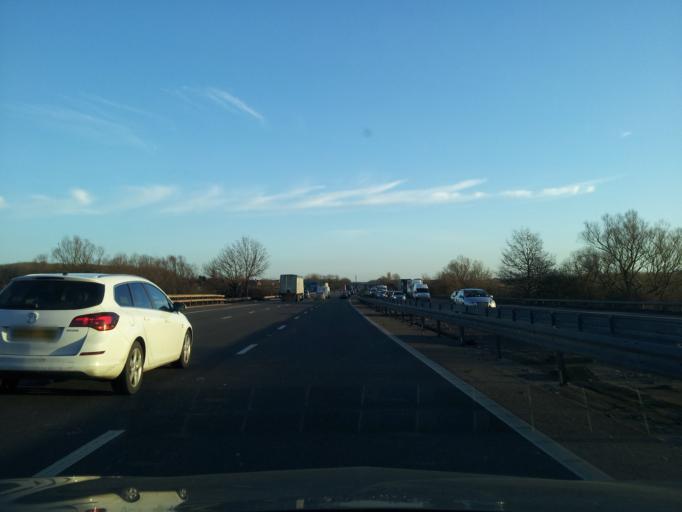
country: GB
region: England
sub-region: Milton Keynes
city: Gayhurst
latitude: 52.0941
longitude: -0.7590
